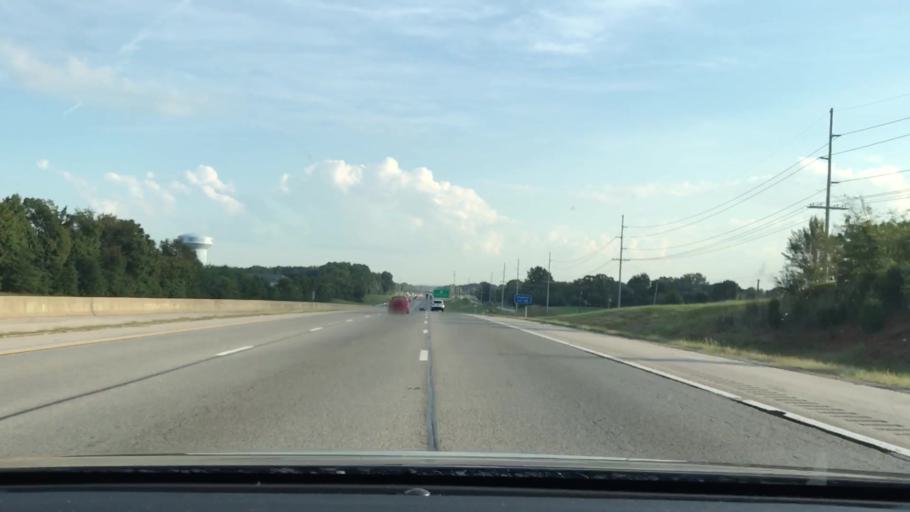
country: US
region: Kentucky
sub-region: Warren County
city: Bowling Green
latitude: 36.9640
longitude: -86.3981
